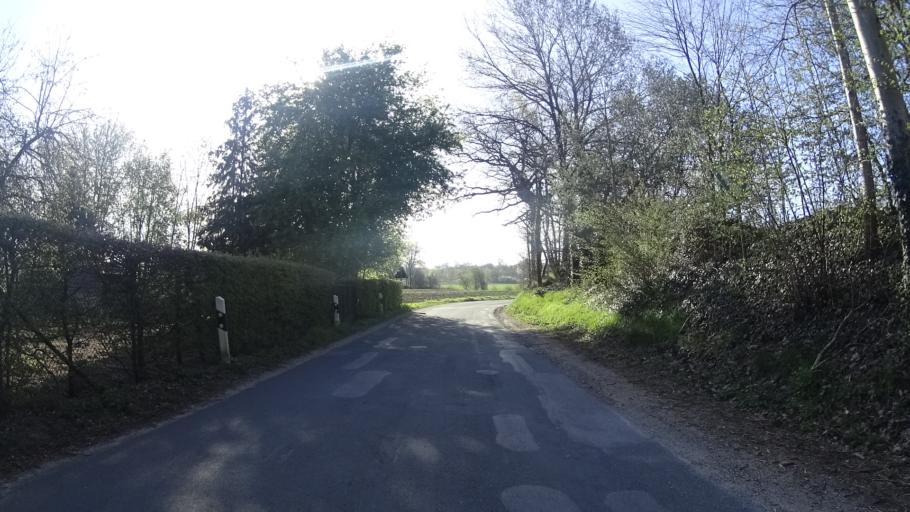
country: DE
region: North Rhine-Westphalia
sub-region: Regierungsbezirk Munster
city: Greven
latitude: 52.0757
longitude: 7.6066
